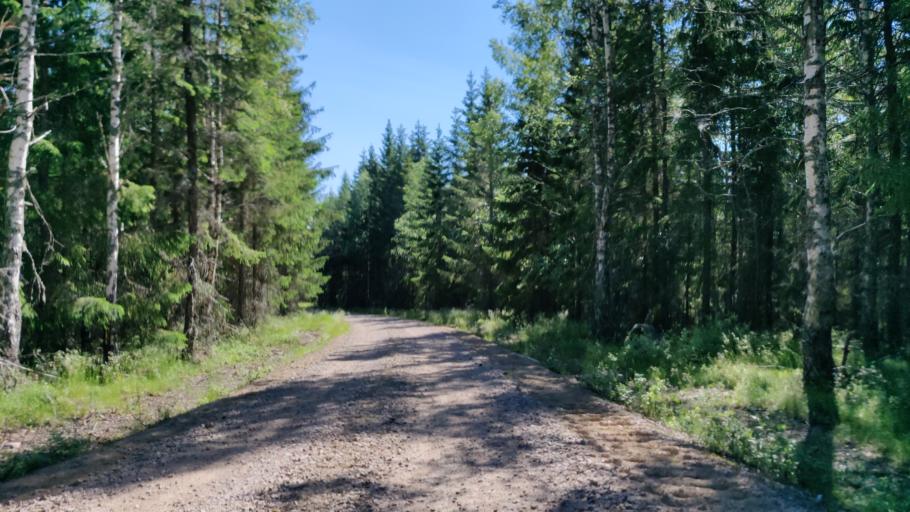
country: SE
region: Vaermland
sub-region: Hagfors Kommun
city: Hagfors
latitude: 59.9815
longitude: 13.5978
